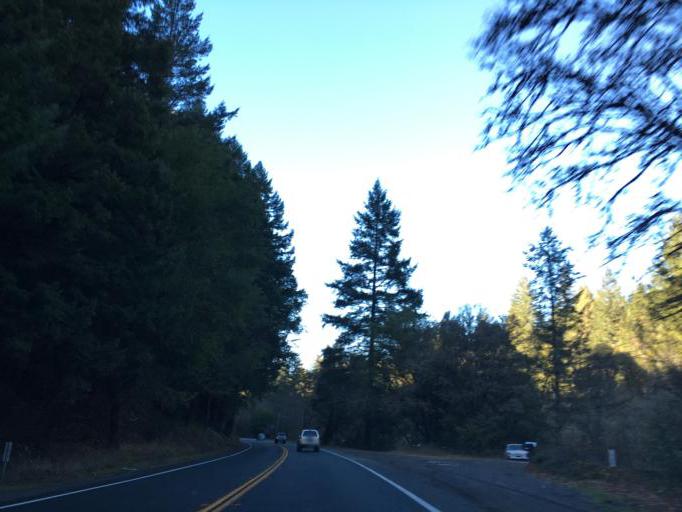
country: US
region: California
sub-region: Mendocino County
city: Brooktrails
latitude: 39.5059
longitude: -123.3806
